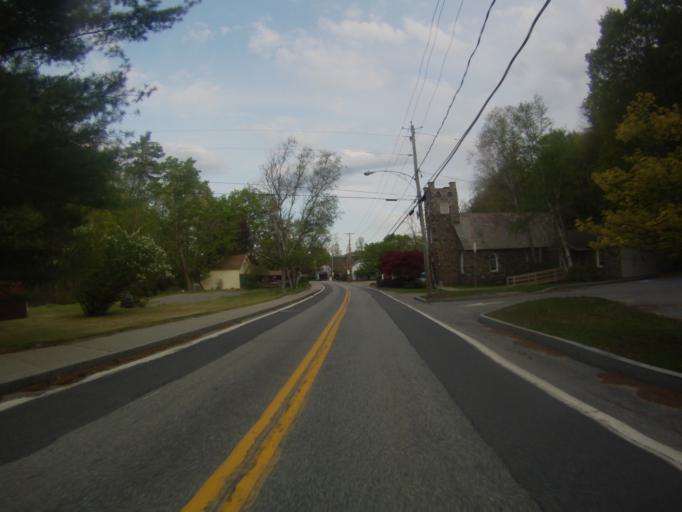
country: US
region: New York
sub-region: Essex County
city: Ticonderoga
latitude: 43.7472
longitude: -73.5008
